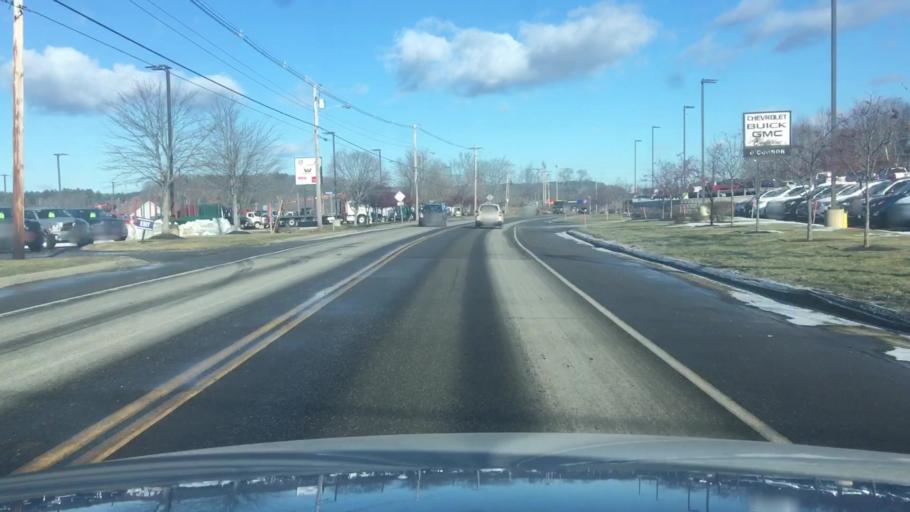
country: US
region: Maine
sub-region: Kennebec County
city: Augusta
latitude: 44.3296
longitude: -69.7626
